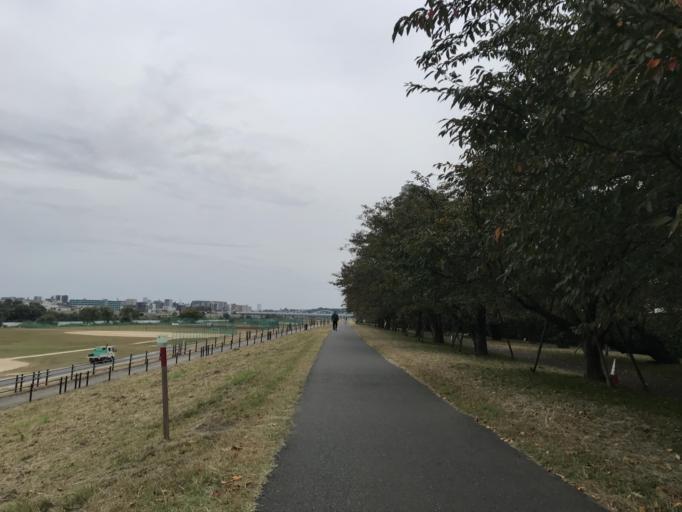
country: JP
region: Kanagawa
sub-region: Kawasaki-shi
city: Kawasaki
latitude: 35.5686
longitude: 139.6781
